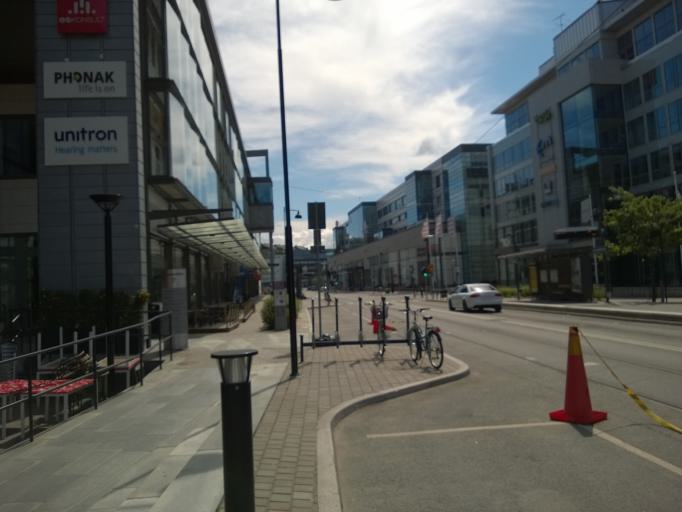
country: SE
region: Stockholm
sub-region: Sundbybergs Kommun
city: Sundbyberg
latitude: 59.3598
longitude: 17.9790
